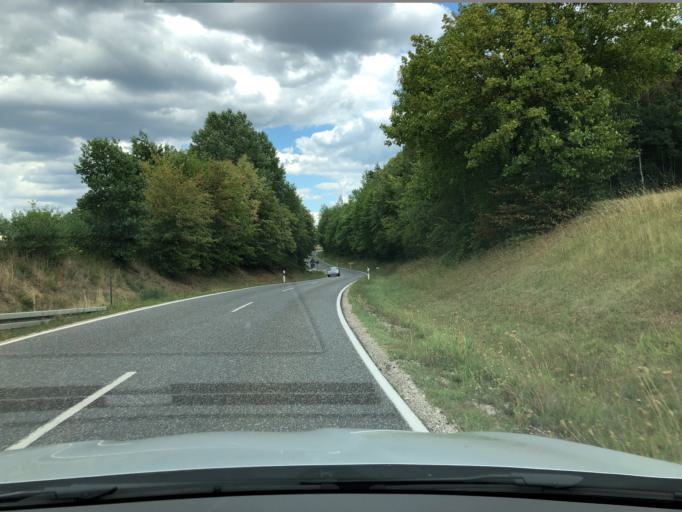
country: DE
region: Bavaria
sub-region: Upper Palatinate
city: Poppenricht
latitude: 49.4907
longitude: 11.8116
